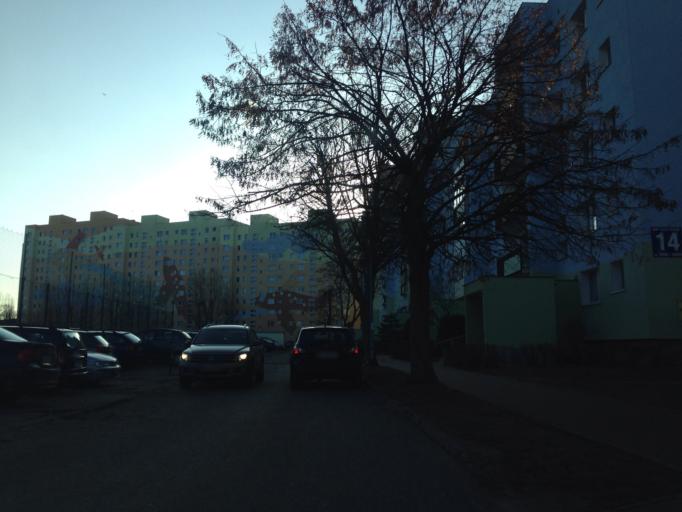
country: PL
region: Pomeranian Voivodeship
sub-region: Gdansk
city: Gdansk
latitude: 54.3942
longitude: 18.6087
